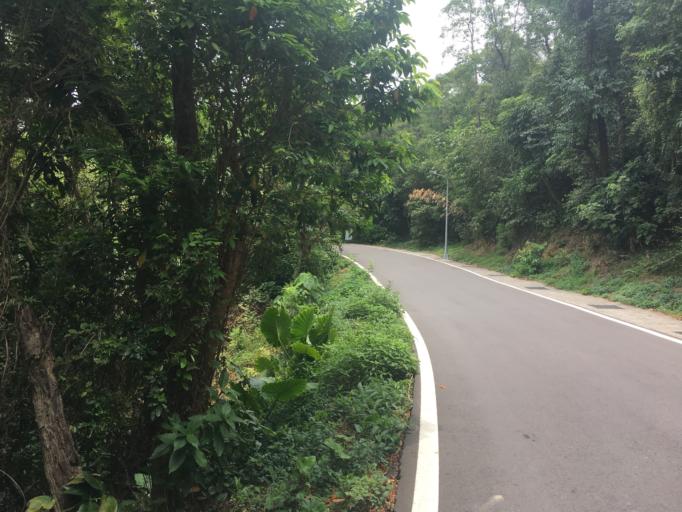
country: TW
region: Taipei
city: Taipei
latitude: 25.0893
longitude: 121.5527
